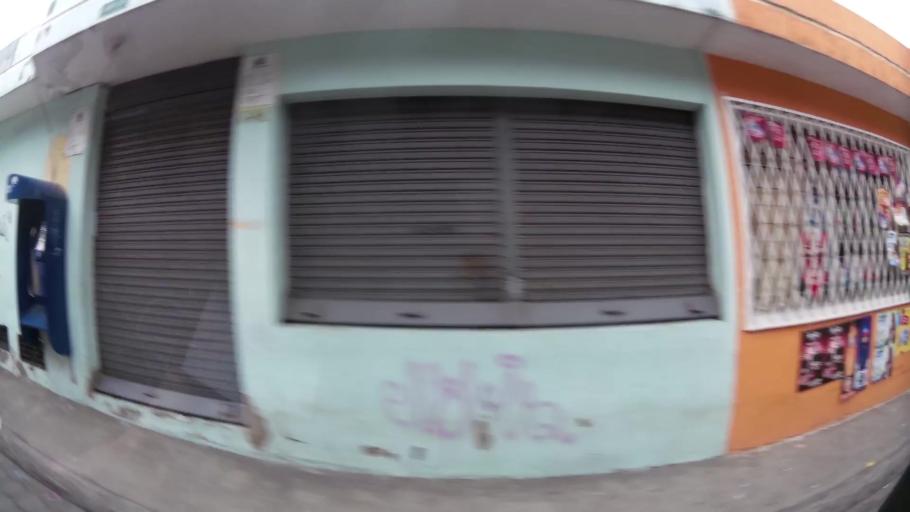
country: EC
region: Pichincha
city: Quito
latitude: -0.3121
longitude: -78.5463
